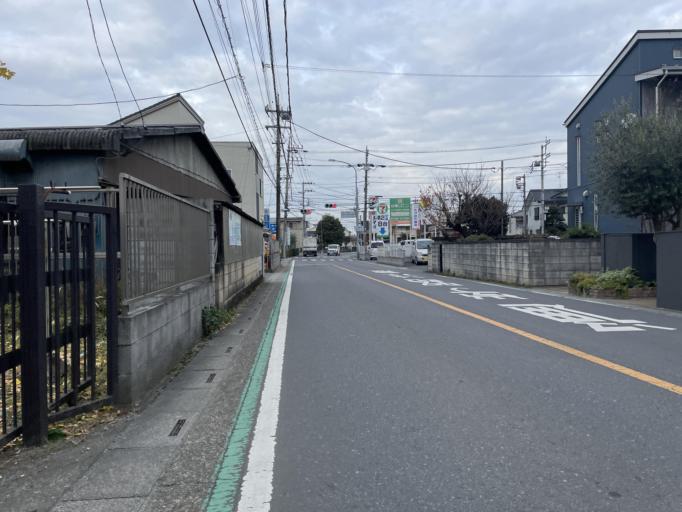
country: JP
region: Saitama
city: Shiraoka
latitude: 36.0111
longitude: 139.6608
